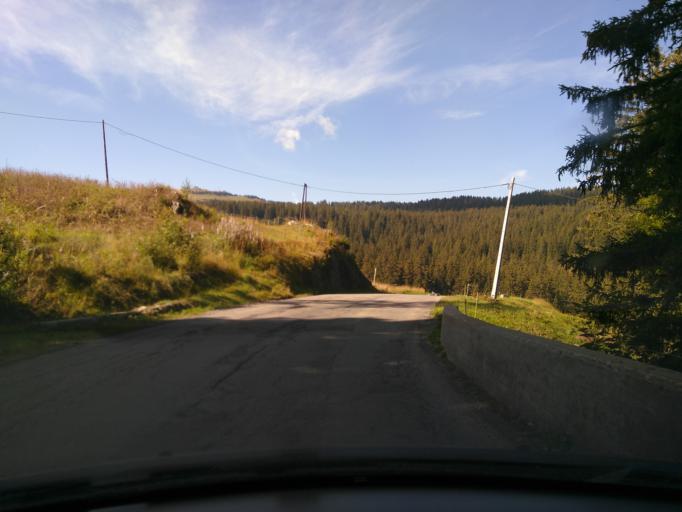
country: FR
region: Rhone-Alpes
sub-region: Departement de la Savoie
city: Beaufort
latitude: 45.7688
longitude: 6.5303
